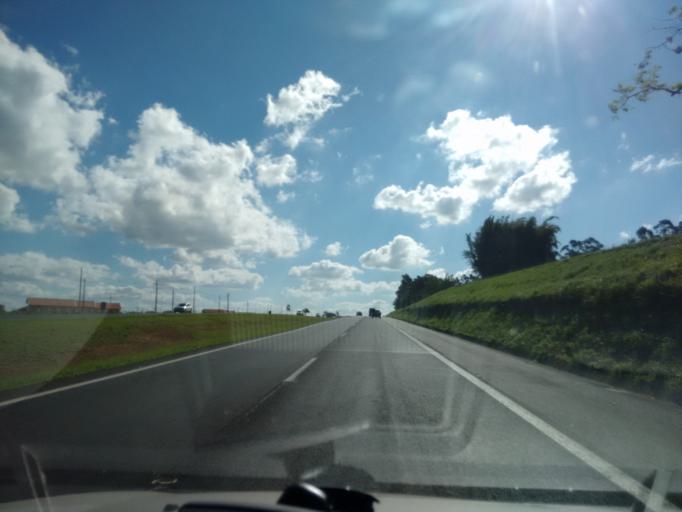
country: BR
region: Sao Paulo
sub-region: Ibate
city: Ibate
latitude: -21.9717
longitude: -47.9471
